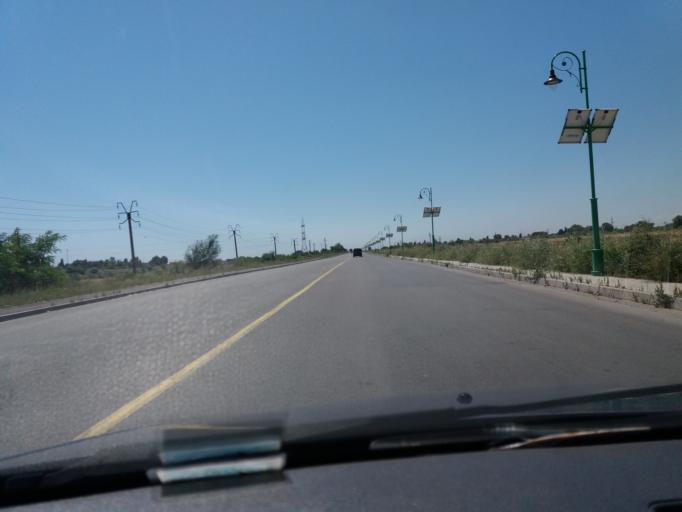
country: RO
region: Constanta
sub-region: Comuna Navodari
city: Navodari
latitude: 44.3053
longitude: 28.6150
